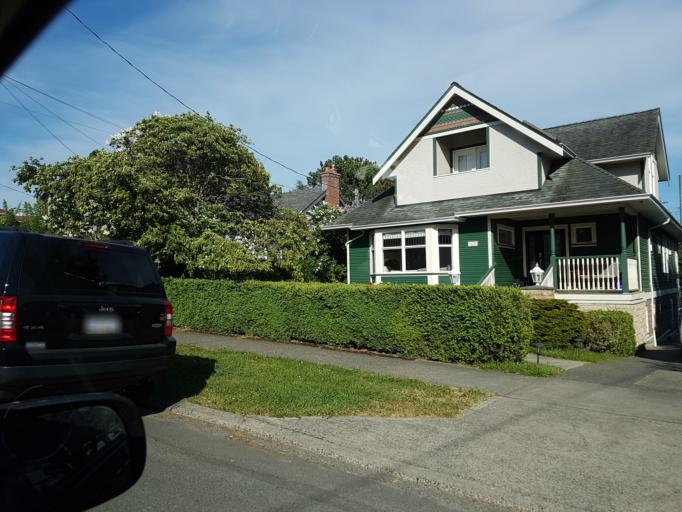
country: CA
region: British Columbia
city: Oak Bay
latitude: 48.4372
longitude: -123.3028
